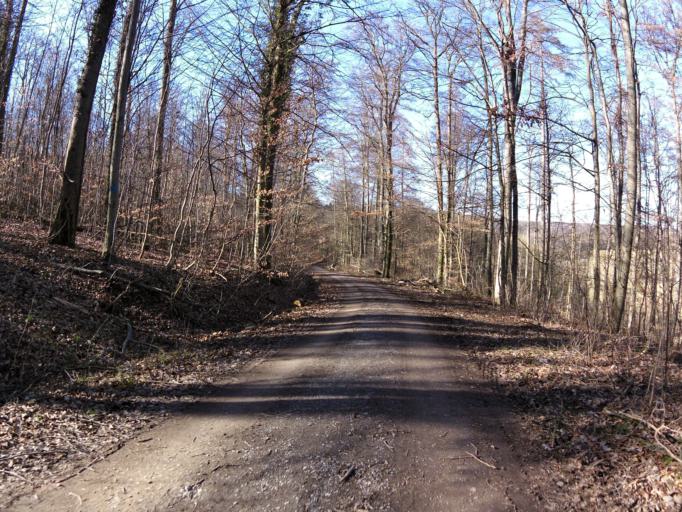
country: DE
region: Bavaria
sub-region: Regierungsbezirk Unterfranken
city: Estenfeld
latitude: 49.8571
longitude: 9.9948
